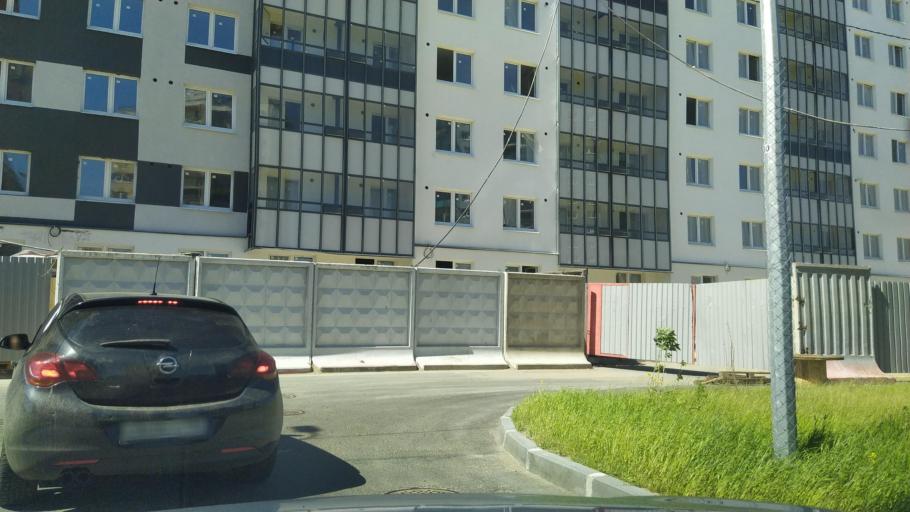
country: RU
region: St.-Petersburg
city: Krasnogvargeisky
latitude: 60.0012
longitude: 30.4524
